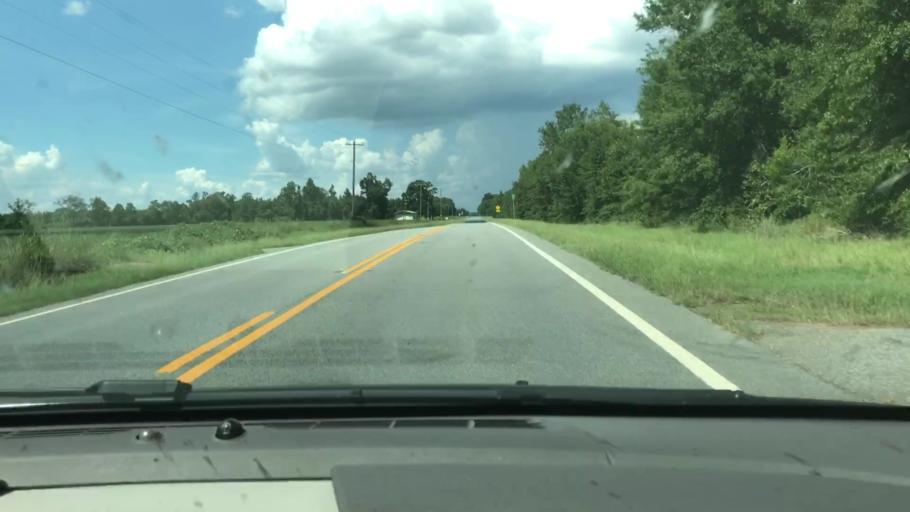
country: US
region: Georgia
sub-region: Quitman County
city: Georgetown
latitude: 31.7929
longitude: -85.0922
